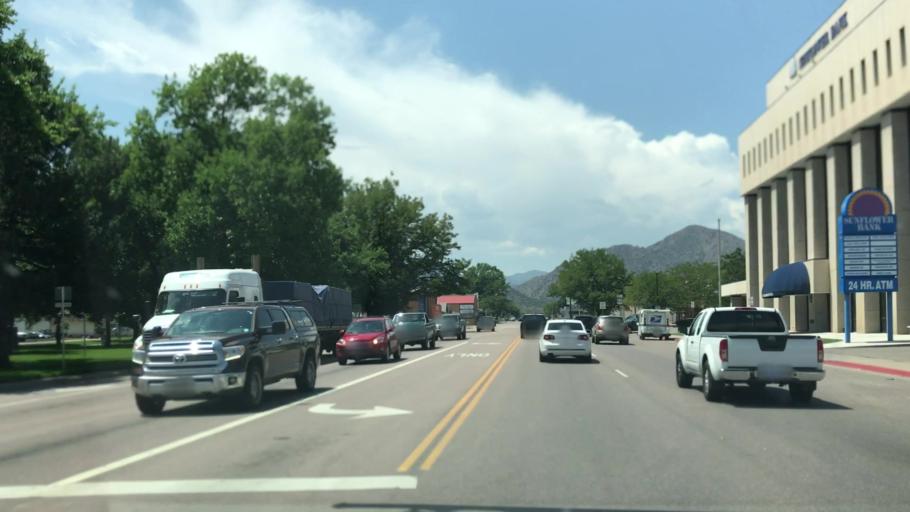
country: US
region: Colorado
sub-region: Fremont County
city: Canon City
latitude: 38.4422
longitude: -105.2350
